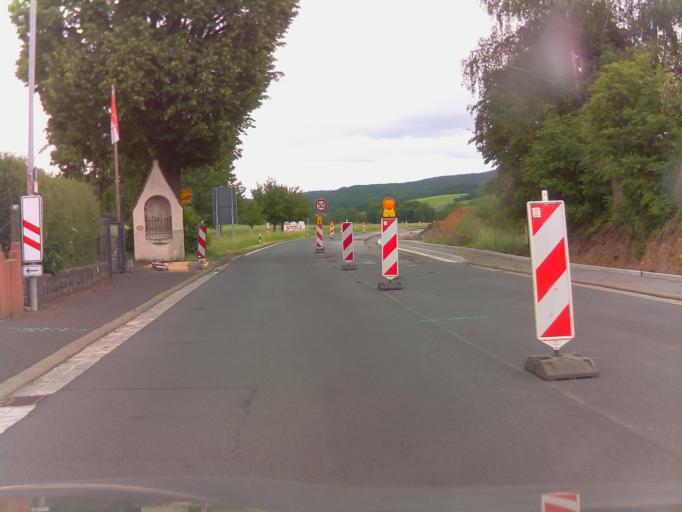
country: DE
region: Bavaria
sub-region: Regierungsbezirk Unterfranken
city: Sondheim vor der Rhoen
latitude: 50.4811
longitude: 10.1798
